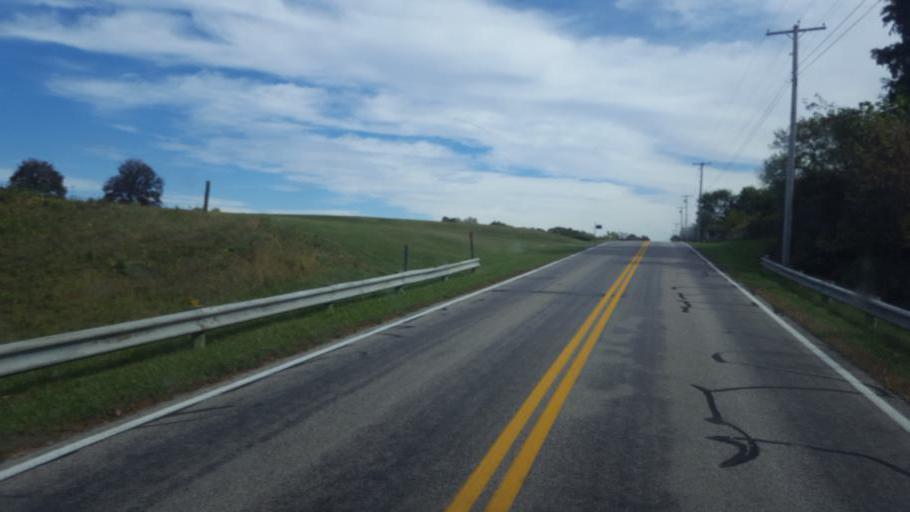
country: US
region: Ohio
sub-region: Erie County
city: Huron
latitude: 41.3648
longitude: -82.4838
